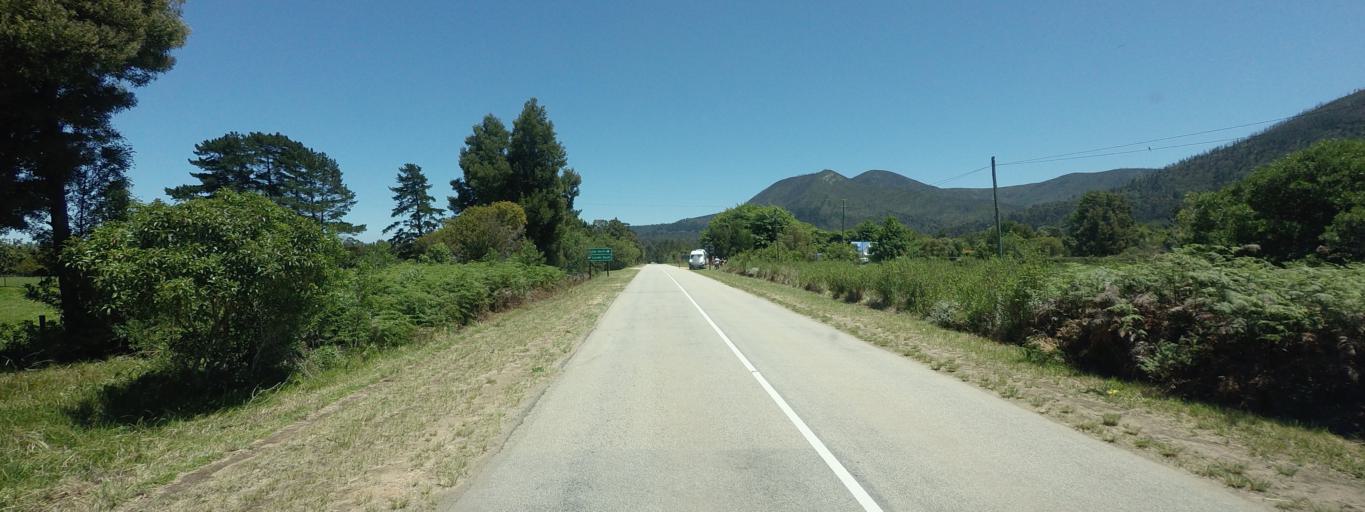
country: ZA
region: Western Cape
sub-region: Eden District Municipality
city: Plettenberg Bay
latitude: -33.9368
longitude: 23.5045
